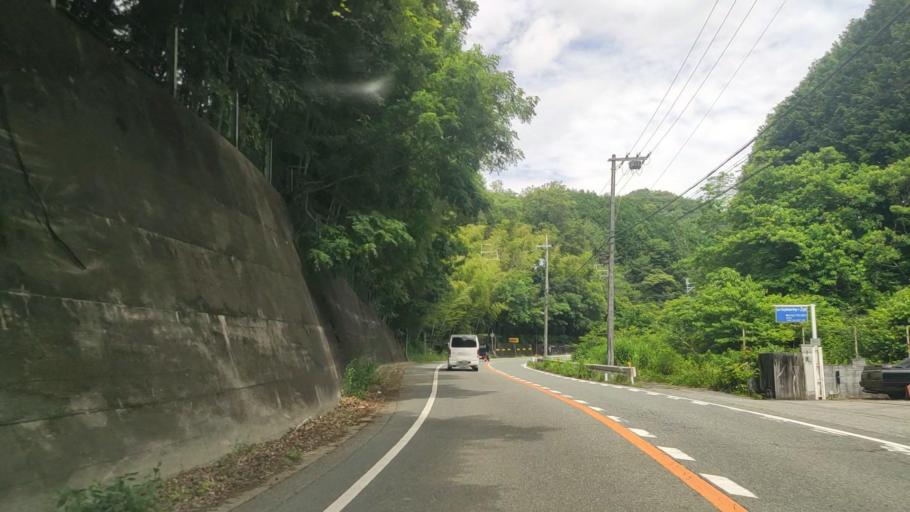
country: JP
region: Hyogo
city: Yamazakicho-nakabirose
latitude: 34.9909
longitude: 134.4054
